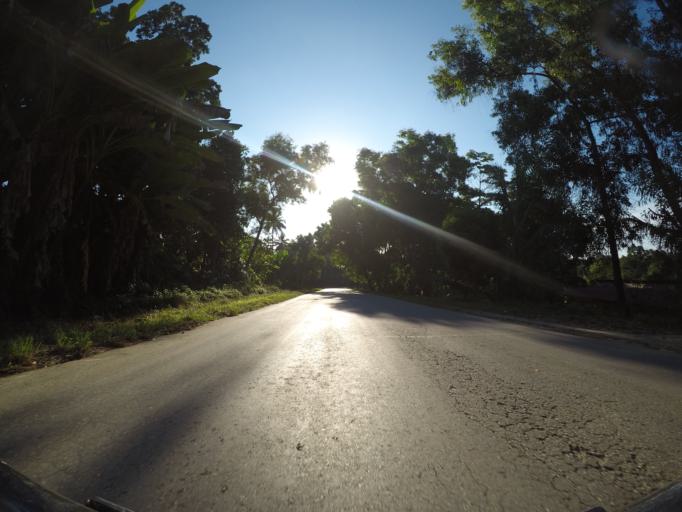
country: TZ
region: Pemba South
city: Uwelini
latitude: -5.3784
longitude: 39.6770
